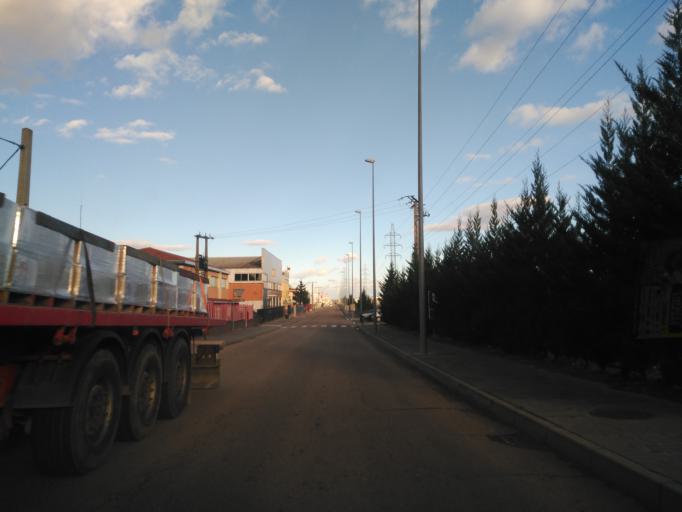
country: ES
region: Castille and Leon
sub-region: Provincia de Salamanca
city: Carbajosa de la Sagrada
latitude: 40.9419
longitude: -5.6674
